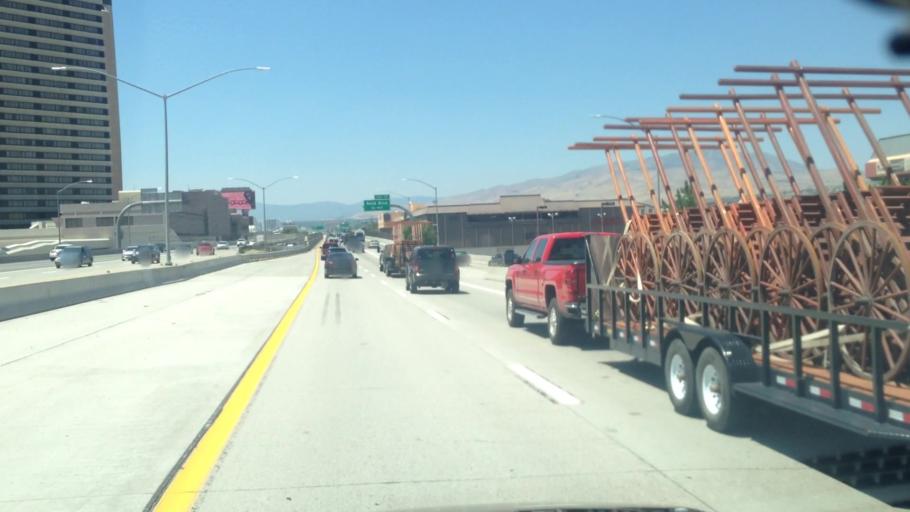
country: US
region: Nevada
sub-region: Washoe County
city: Sparks
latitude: 39.5349
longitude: -119.7558
